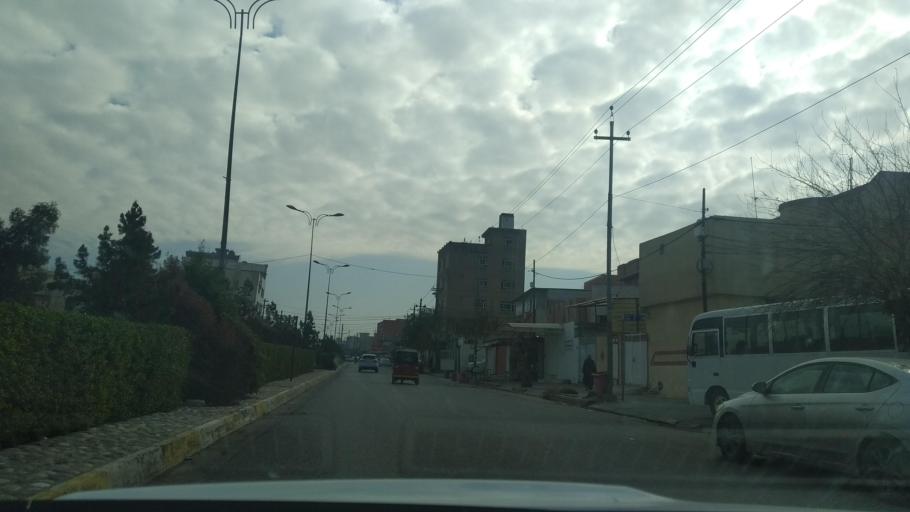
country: IQ
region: Arbil
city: Erbil
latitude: 36.1782
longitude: 44.0285
